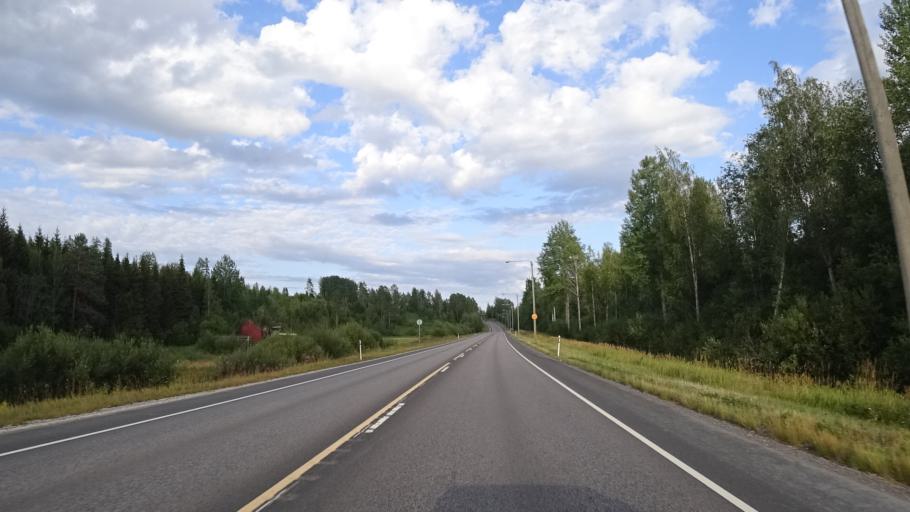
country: FI
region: South Karelia
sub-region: Imatra
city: Simpele
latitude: 61.4259
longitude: 29.3737
